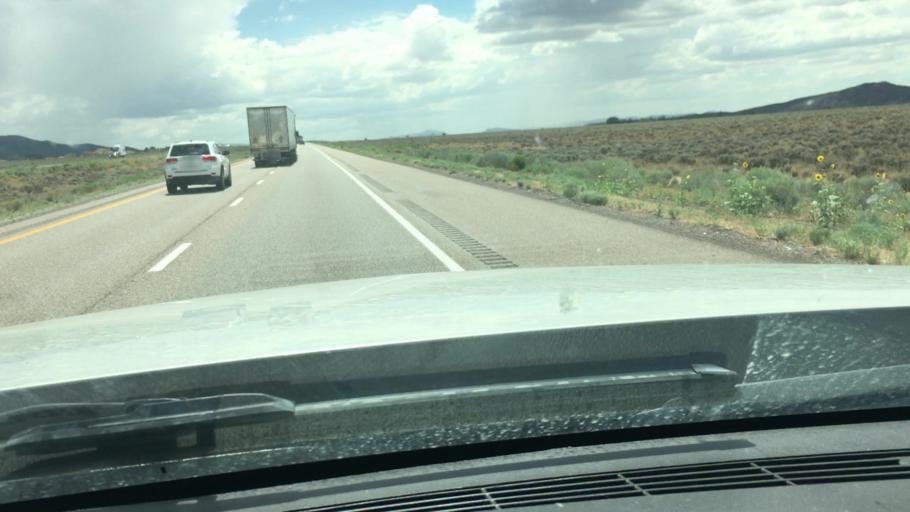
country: US
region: Utah
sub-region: Iron County
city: Parowan
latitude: 37.8207
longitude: -112.9160
